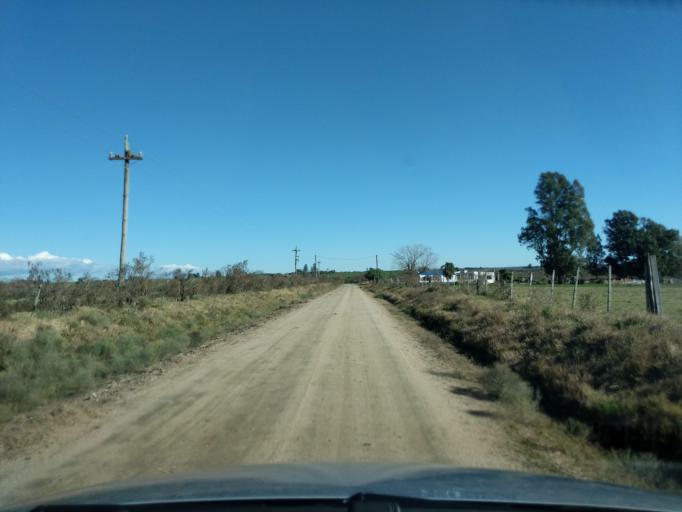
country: UY
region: Florida
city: Florida
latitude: -34.0796
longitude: -56.2630
